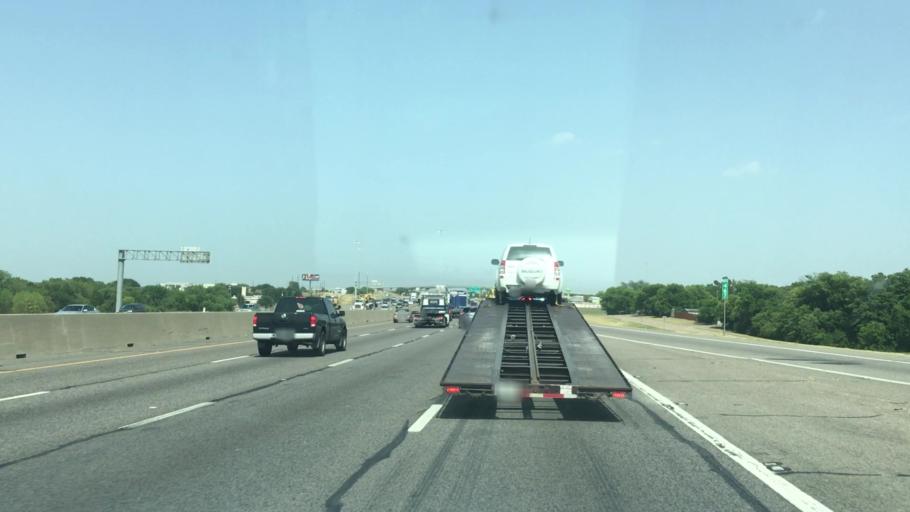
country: US
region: Texas
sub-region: Dallas County
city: DeSoto
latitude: 32.6420
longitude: -96.8358
